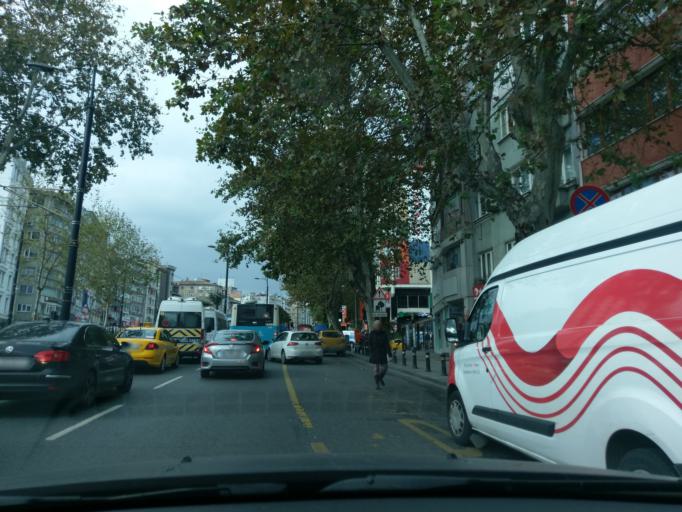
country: TR
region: Istanbul
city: Istanbul
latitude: 41.0116
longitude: 28.9415
